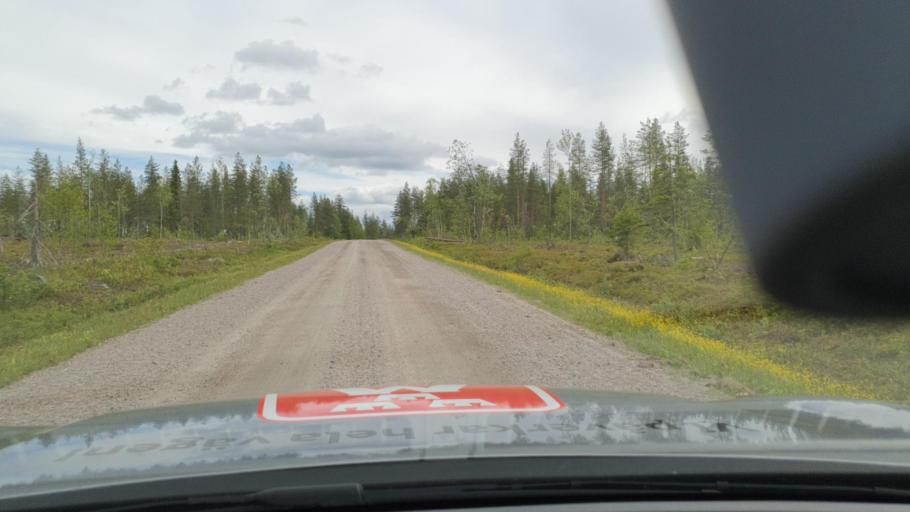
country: FI
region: Lapland
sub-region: Torniolaakso
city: Ylitornio
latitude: 65.9586
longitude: 23.6182
